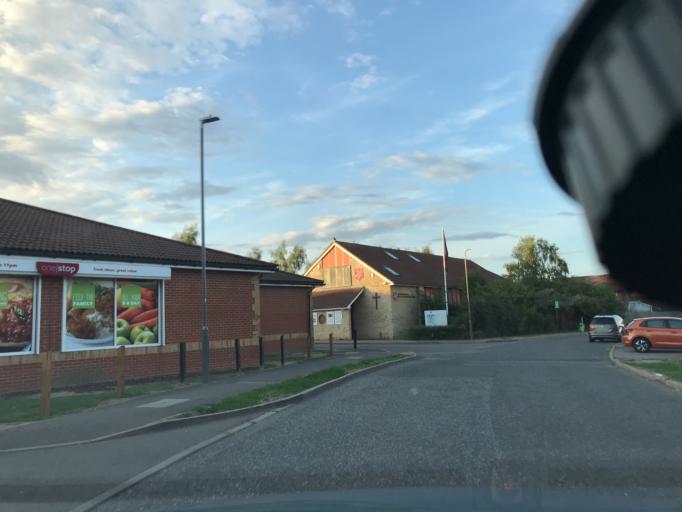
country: GB
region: England
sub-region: Buckinghamshire
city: Aylesbury
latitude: 51.8223
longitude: -0.7937
